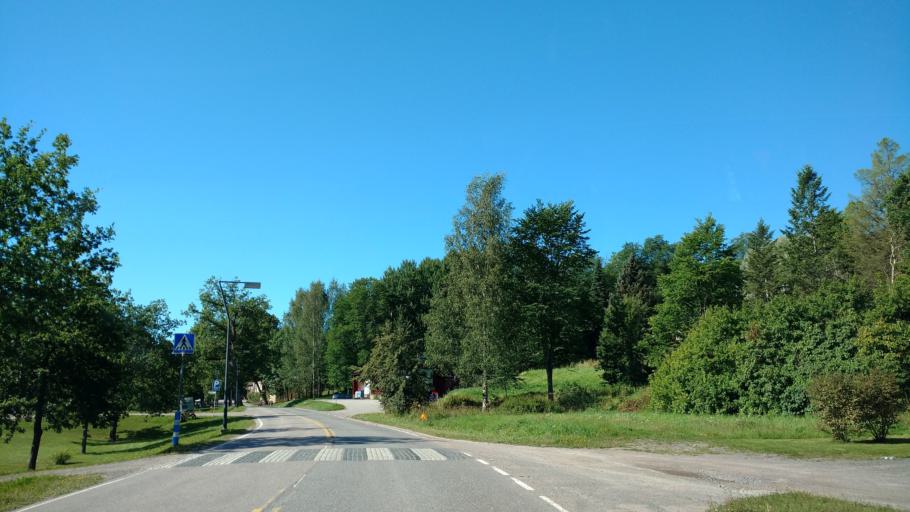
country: FI
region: Uusimaa
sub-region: Raaseporin
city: Pohja
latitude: 60.1319
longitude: 23.5450
